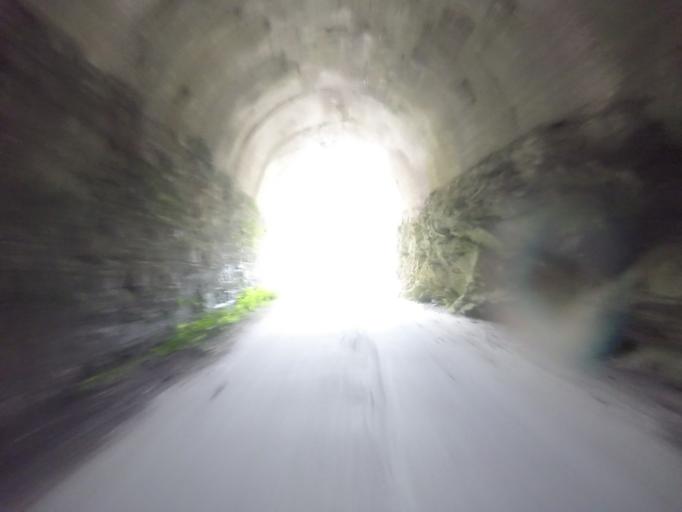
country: ES
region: Navarre
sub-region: Provincia de Navarra
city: Areso
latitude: 43.1175
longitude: -1.9375
